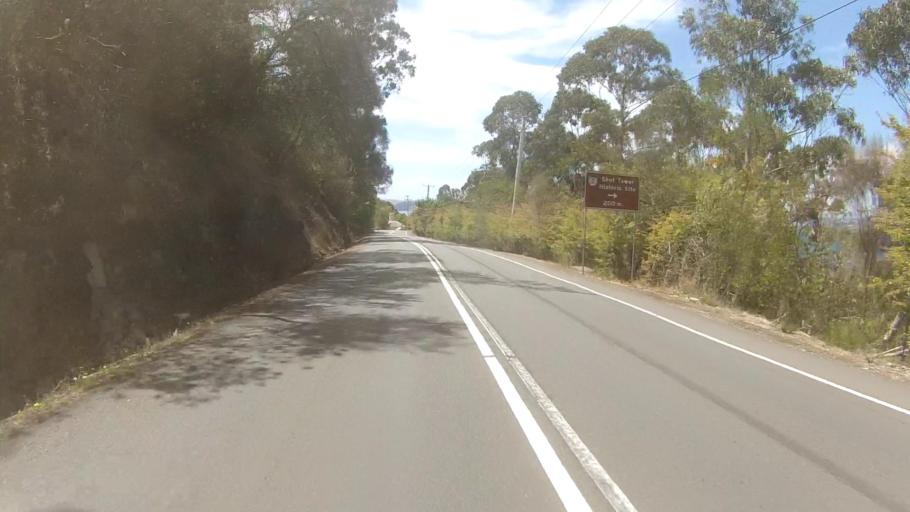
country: AU
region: Tasmania
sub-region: Kingborough
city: Taroona
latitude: -42.9593
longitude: 147.3347
